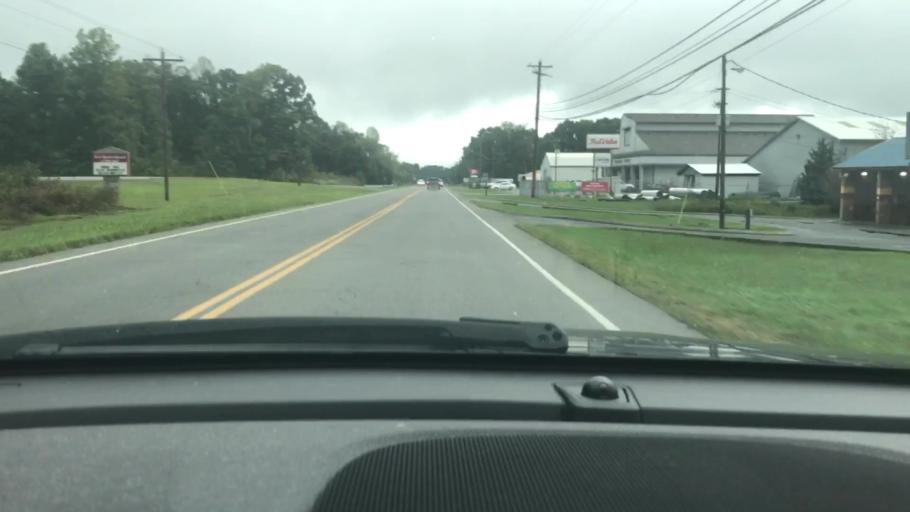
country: US
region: Tennessee
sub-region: Dickson County
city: White Bluff
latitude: 36.1049
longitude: -87.1948
